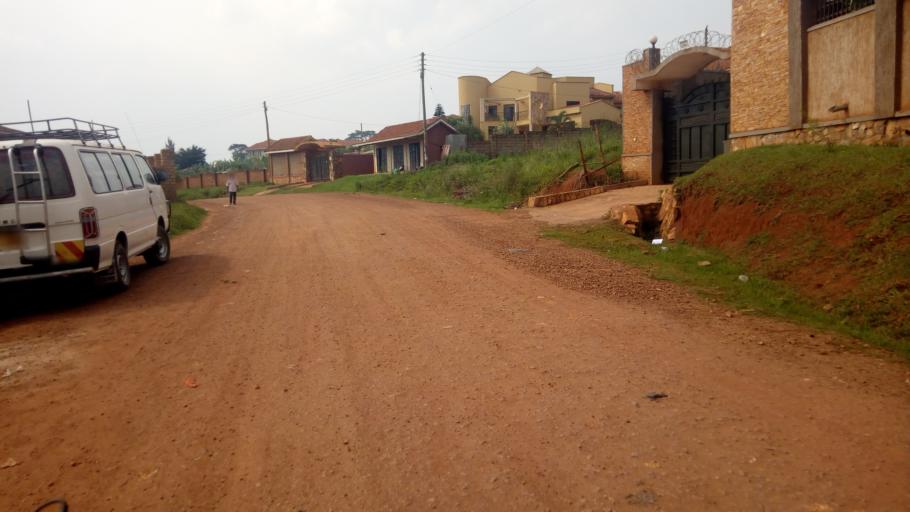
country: UG
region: Central Region
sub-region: Wakiso District
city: Kireka
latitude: 0.3150
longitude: 32.6537
